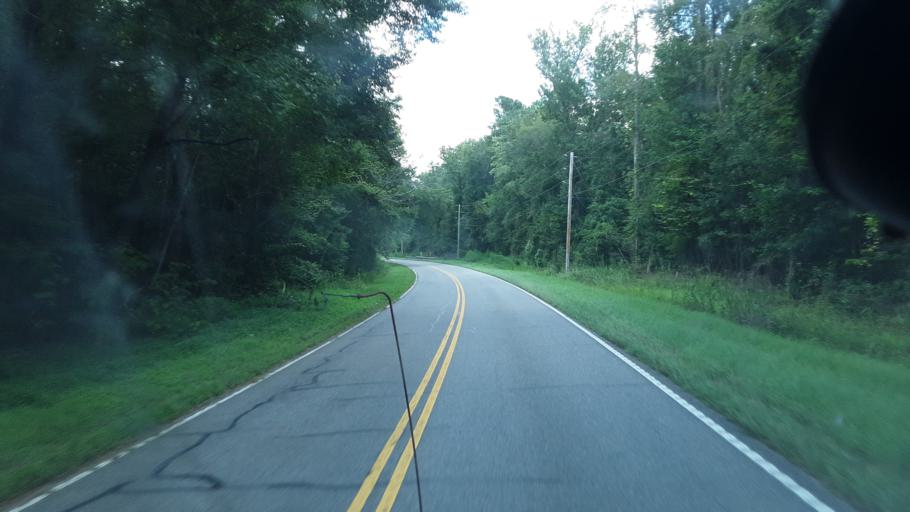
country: US
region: South Carolina
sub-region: Florence County
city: Johnsonville
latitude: 33.6592
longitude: -79.4162
